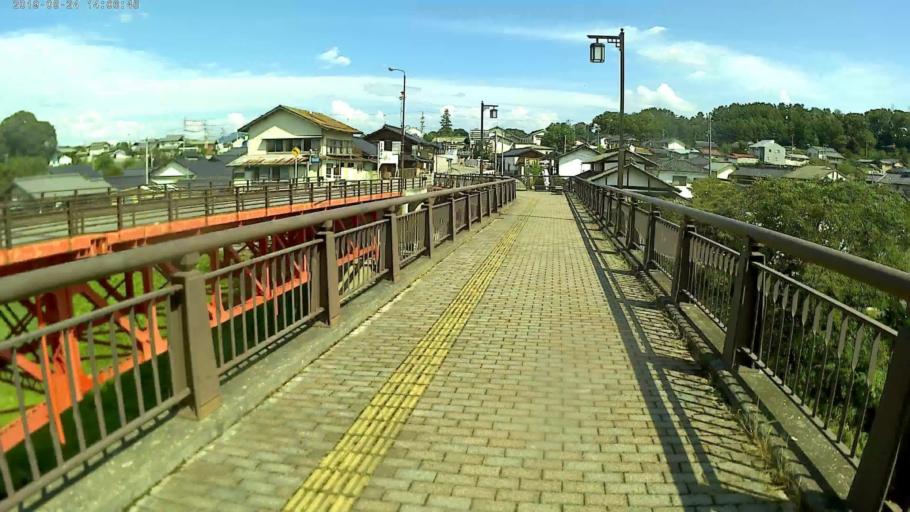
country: JP
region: Nagano
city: Komoro
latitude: 36.2707
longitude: 138.4182
